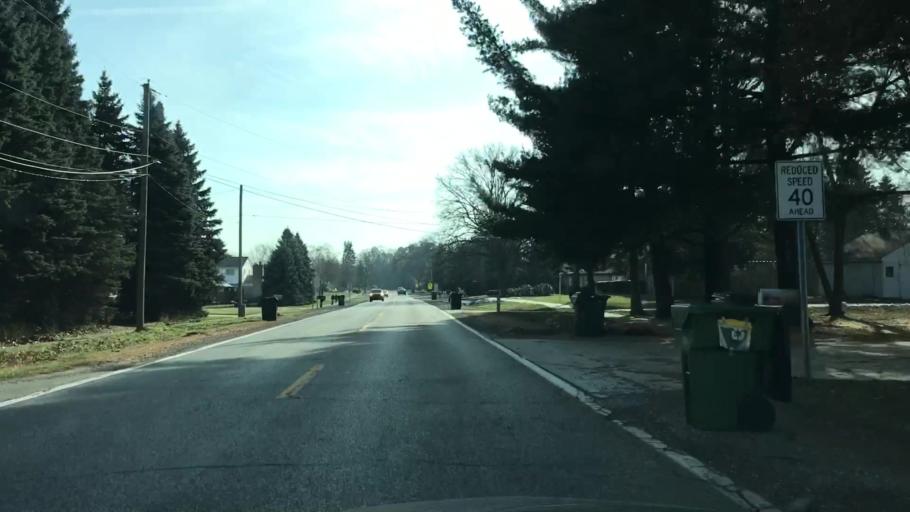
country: US
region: Michigan
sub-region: Macomb County
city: Shelby
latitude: 42.6924
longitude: -83.0695
